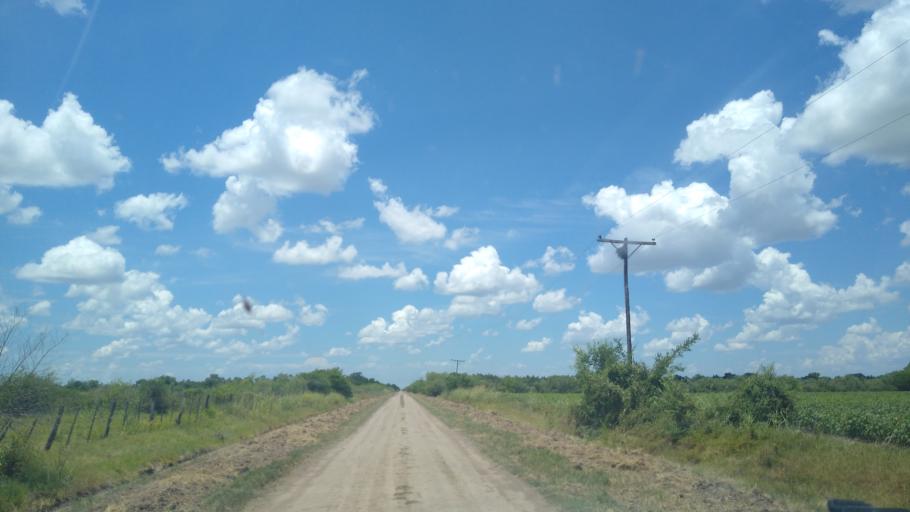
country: AR
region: Chaco
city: Presidencia Roque Saenz Pena
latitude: -26.7359
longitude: -60.3312
